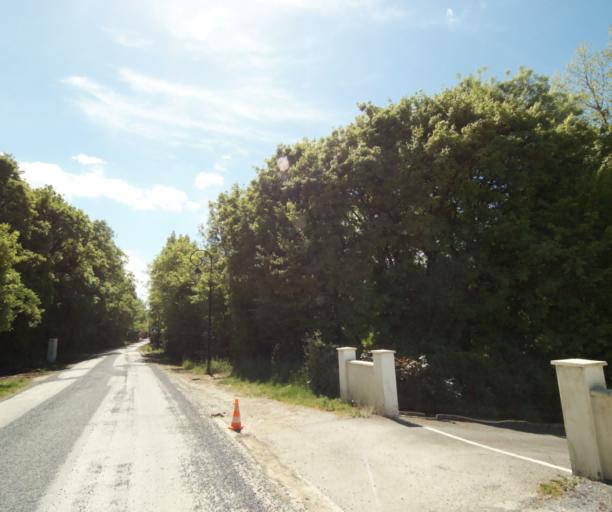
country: FR
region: Poitou-Charentes
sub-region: Departement de la Charente-Maritime
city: Chaniers
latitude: 45.7372
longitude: -0.5067
